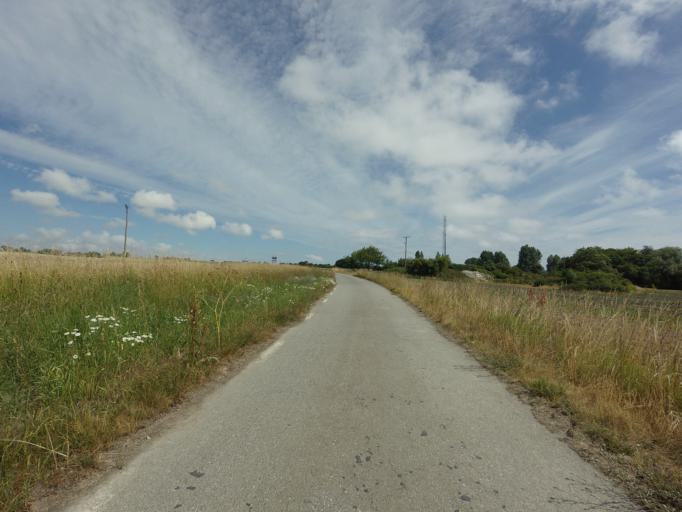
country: SE
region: Skane
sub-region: Simrishamns Kommun
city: Simrishamn
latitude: 55.5098
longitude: 14.3359
